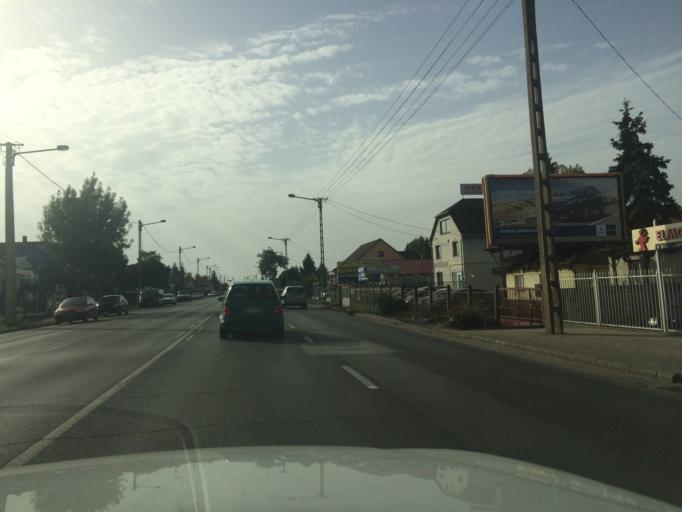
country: HU
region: Szabolcs-Szatmar-Bereg
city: Nyiregyhaza
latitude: 47.9280
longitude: 21.7186
